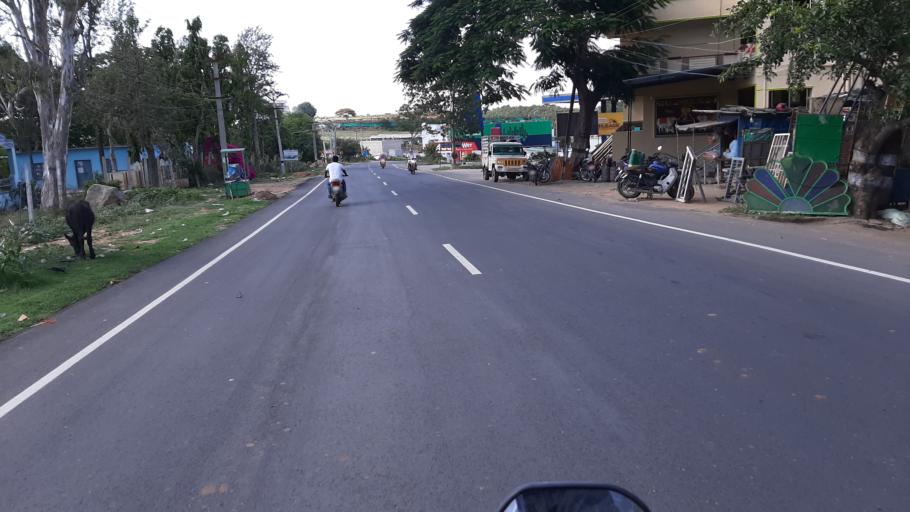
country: IN
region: Tamil Nadu
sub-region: Krishnagiri
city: Denkanikota
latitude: 12.5336
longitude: 77.7880
